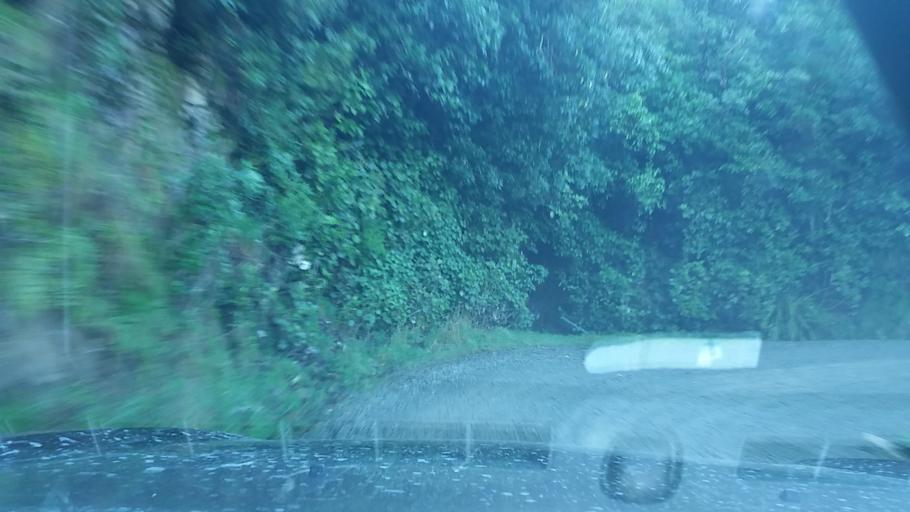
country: NZ
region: Marlborough
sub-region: Marlborough District
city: Picton
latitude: -41.1401
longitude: 174.0470
